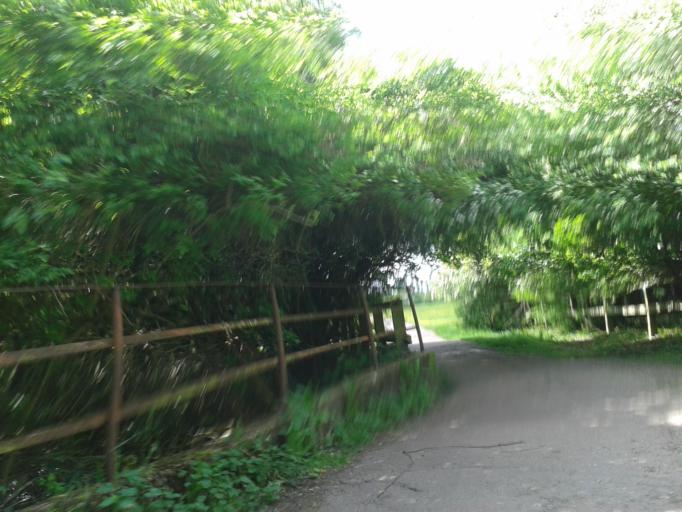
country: GB
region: England
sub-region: Cambridgeshire
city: Cambridge
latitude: 52.2109
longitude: 0.1520
